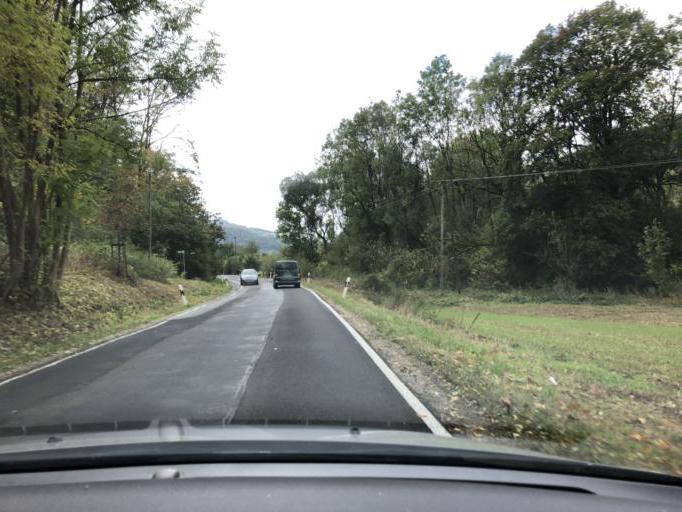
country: DE
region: Thuringia
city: Grossbartloff
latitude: 51.2280
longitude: 10.1988
